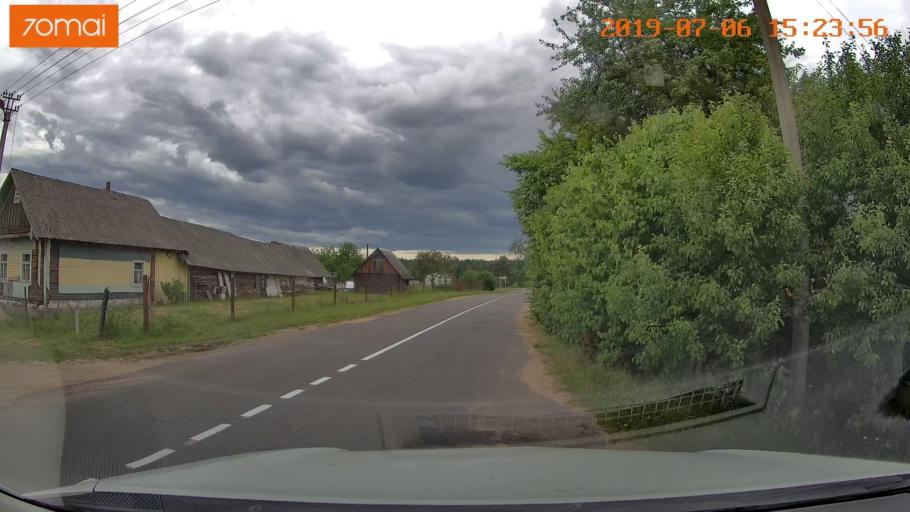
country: BY
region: Minsk
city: Valozhyn
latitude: 54.0165
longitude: 26.6043
